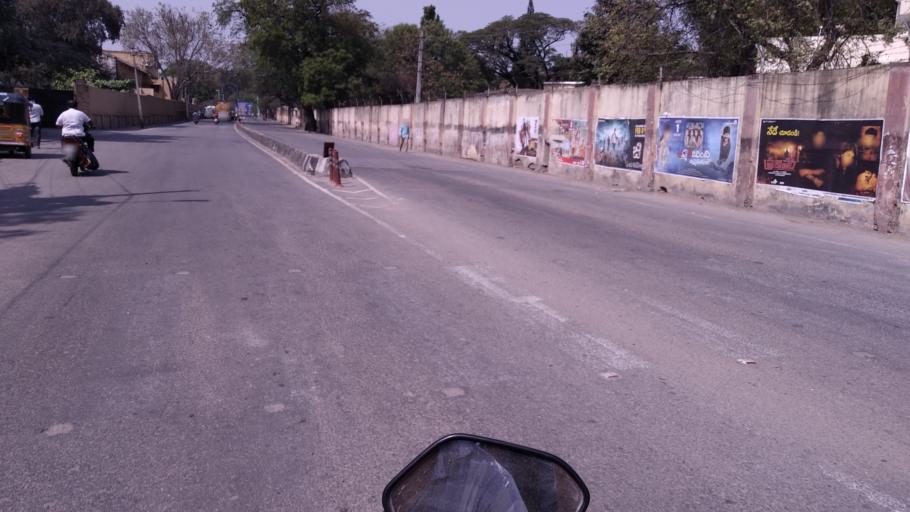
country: IN
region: Telangana
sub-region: Hyderabad
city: Malkajgiri
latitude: 17.4476
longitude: 78.4942
